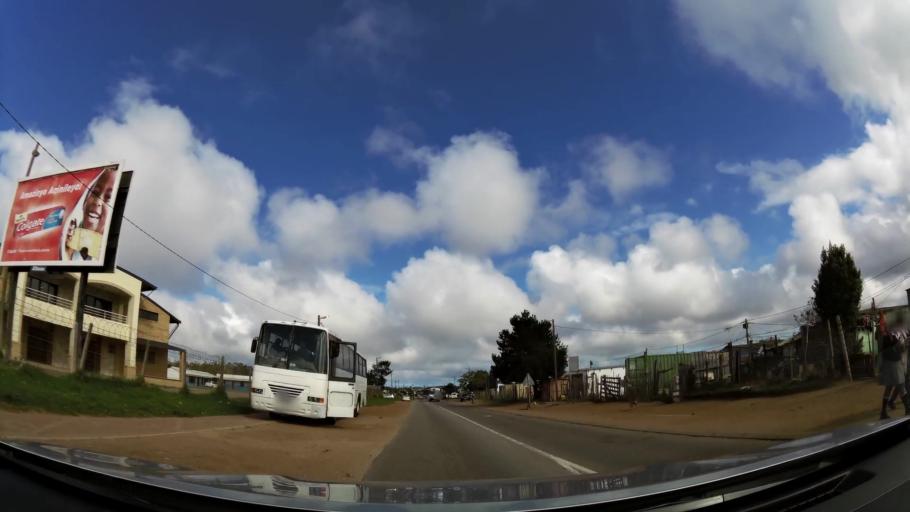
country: ZA
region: Western Cape
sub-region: Eden District Municipality
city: Plettenberg Bay
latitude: -34.0487
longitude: 23.3229
